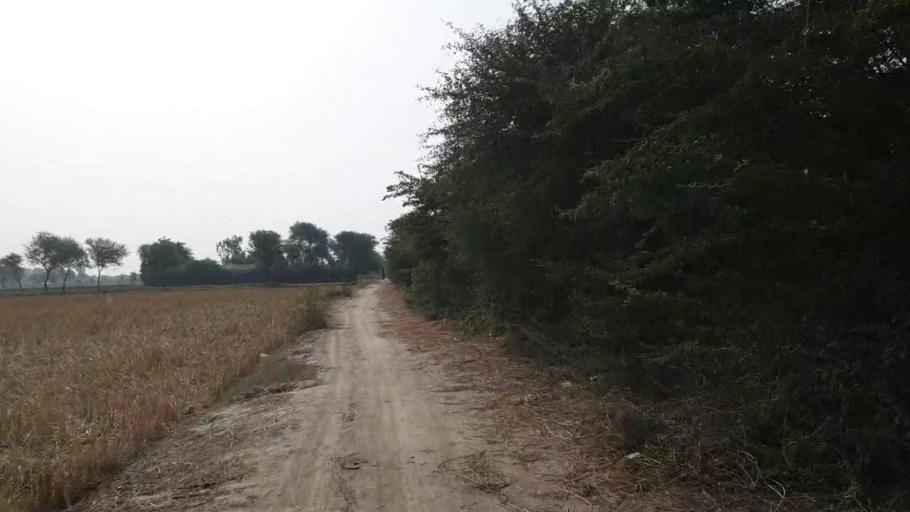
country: PK
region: Sindh
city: Kario
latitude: 24.7786
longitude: 68.5637
